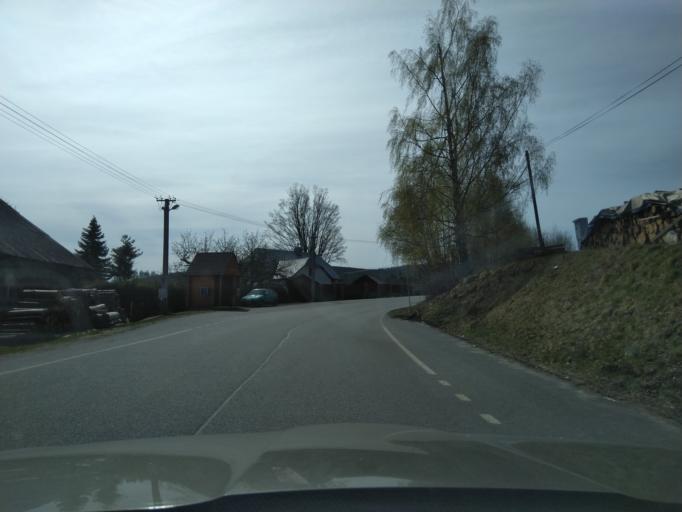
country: CZ
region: Jihocesky
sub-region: Okres Prachatice
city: Stachy
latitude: 49.0862
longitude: 13.6416
